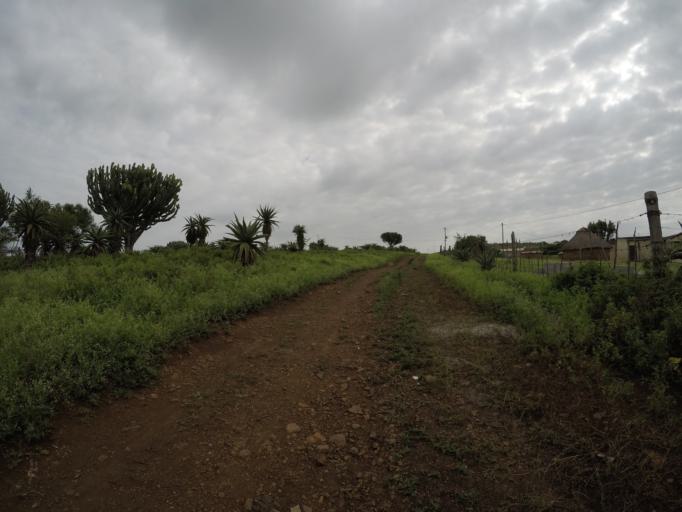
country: ZA
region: KwaZulu-Natal
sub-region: uThungulu District Municipality
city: Empangeni
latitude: -28.6401
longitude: 31.9035
